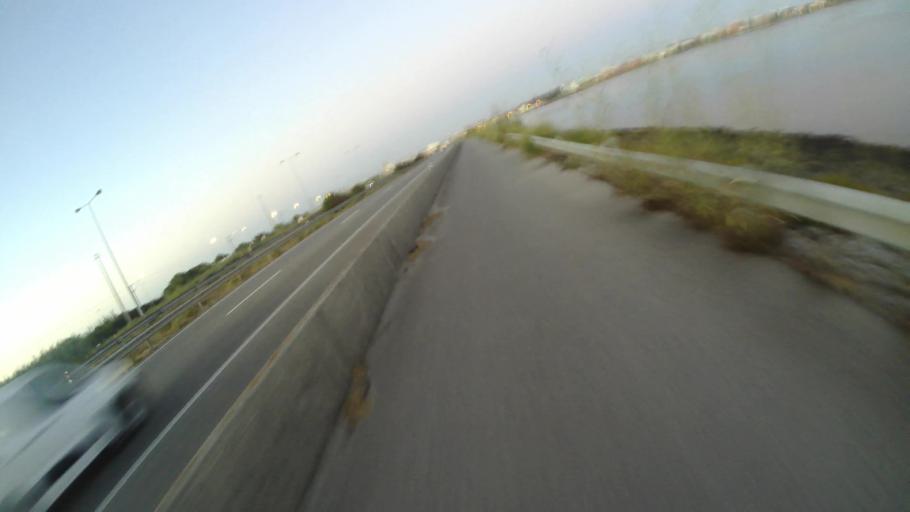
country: PT
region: Aveiro
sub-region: Aveiro
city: Aveiro
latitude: 40.6349
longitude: -8.6728
